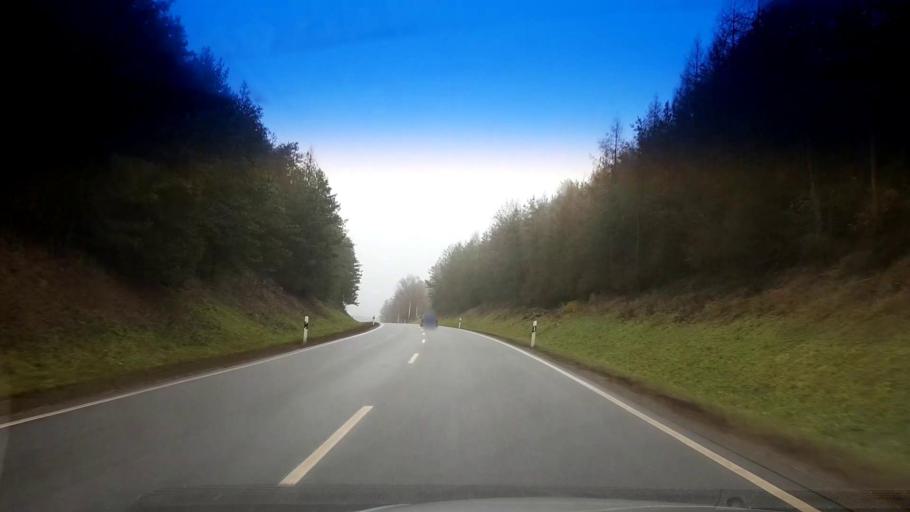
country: DE
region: Bavaria
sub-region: Upper Palatinate
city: Tirschenreuth
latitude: 49.8655
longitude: 12.2606
